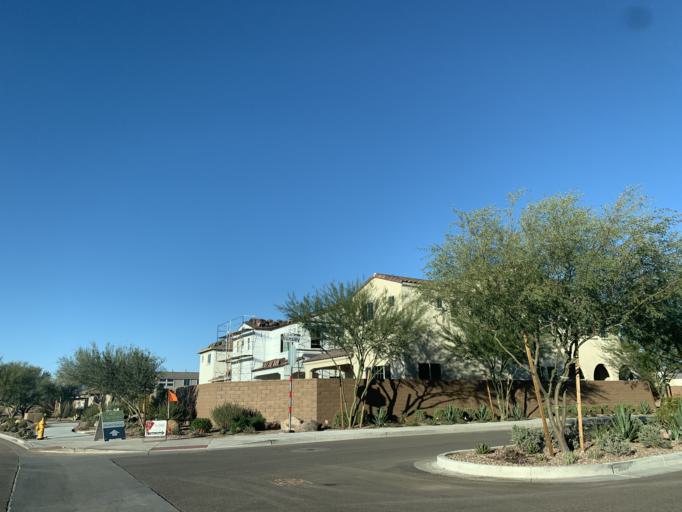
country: US
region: Arizona
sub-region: Maricopa County
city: Cave Creek
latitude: 33.6850
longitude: -112.0138
